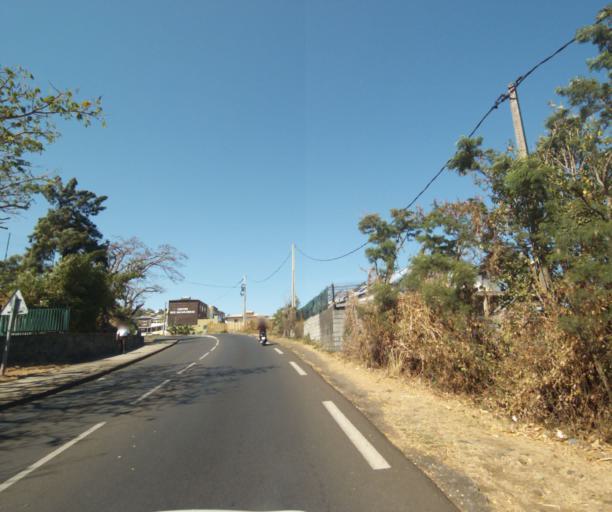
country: RE
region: Reunion
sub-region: Reunion
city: La Possession
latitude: -20.9900
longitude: 55.3302
